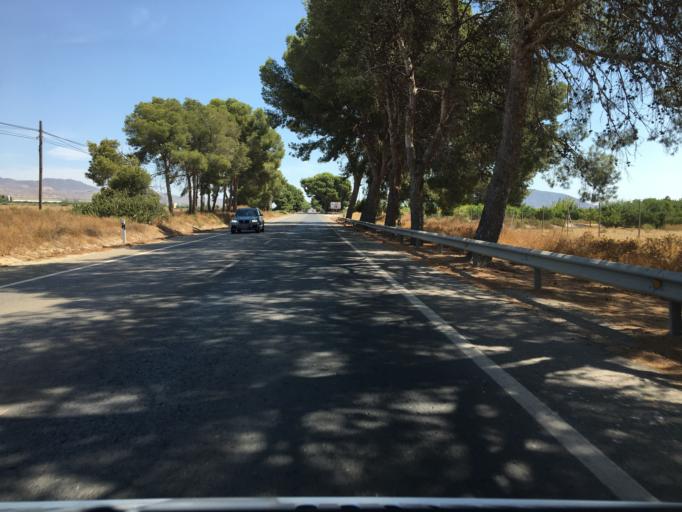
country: ES
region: Andalusia
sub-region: Provincia de Almeria
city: Huercal-Overa
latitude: 37.4193
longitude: -1.9222
